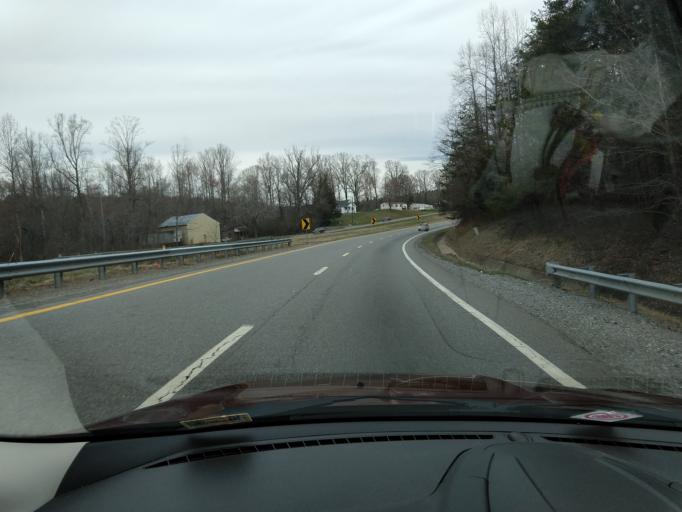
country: US
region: Virginia
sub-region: Franklin County
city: Henry Fork
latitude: 36.8791
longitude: -79.8700
